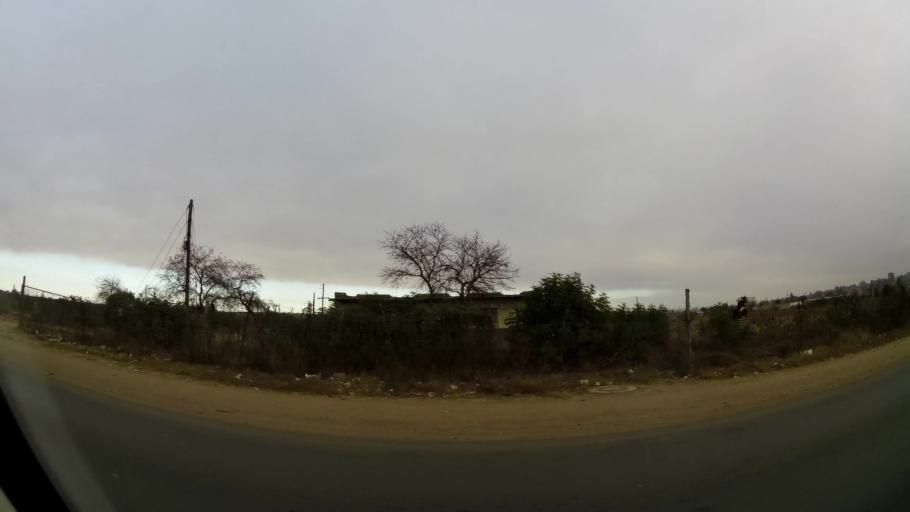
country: ZA
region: Limpopo
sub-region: Capricorn District Municipality
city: Polokwane
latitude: -23.8316
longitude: 29.3795
